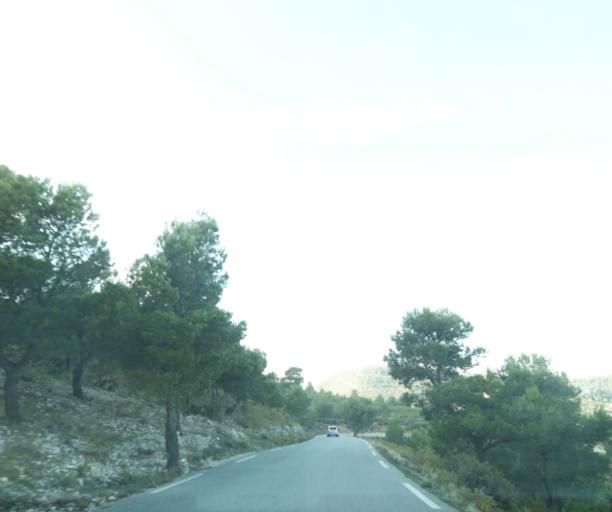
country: FR
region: Provence-Alpes-Cote d'Azur
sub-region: Departement des Bouches-du-Rhone
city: Cassis
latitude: 43.2039
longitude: 5.5655
